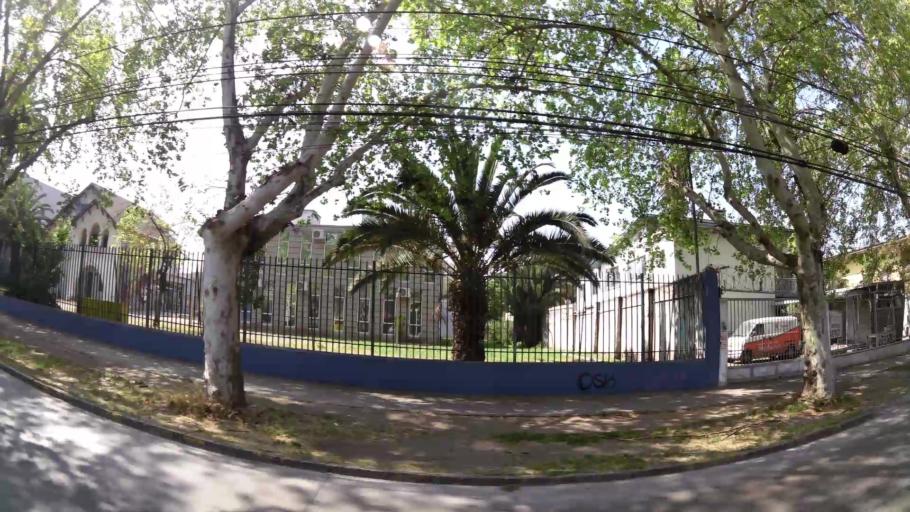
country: CL
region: Santiago Metropolitan
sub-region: Provincia de Santiago
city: Villa Presidente Frei, Nunoa, Santiago, Chile
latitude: -33.4627
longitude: -70.5981
